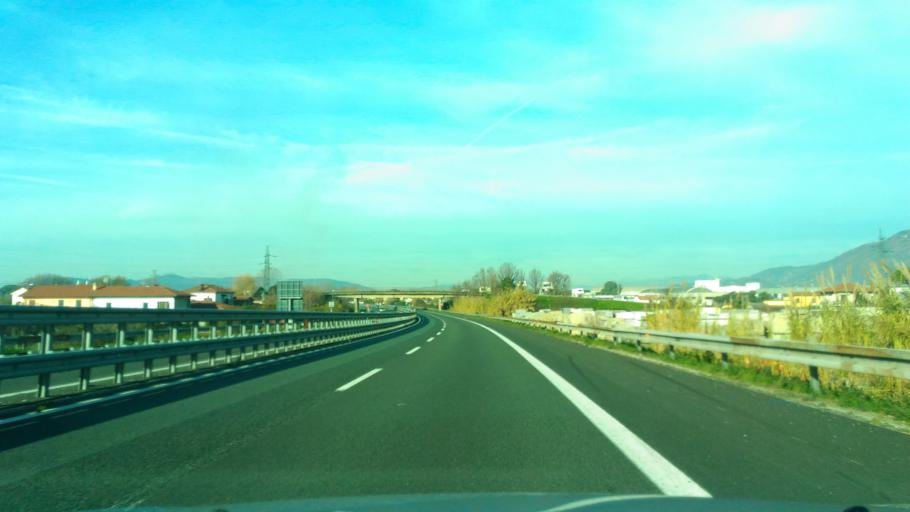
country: IT
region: Tuscany
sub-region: Provincia di Massa-Carrara
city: Massa
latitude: 44.0304
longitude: 10.0884
